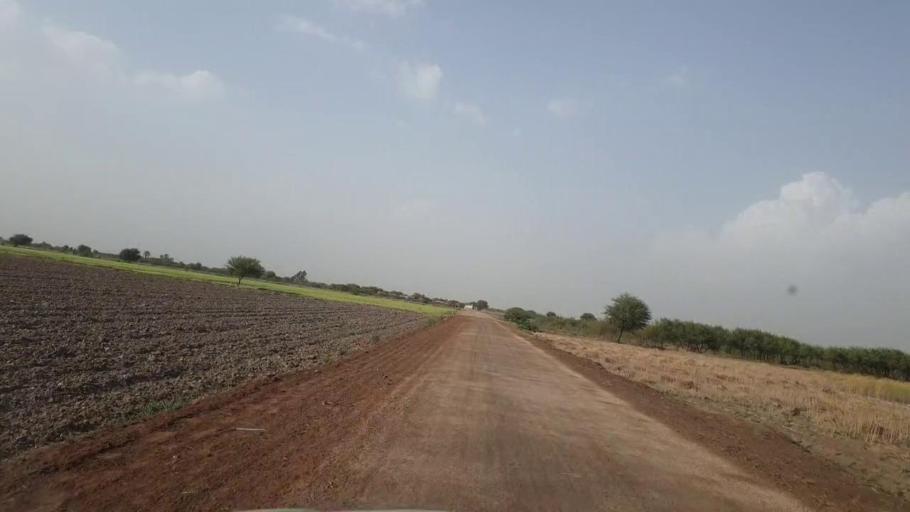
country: PK
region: Sindh
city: Tando Ghulam Ali
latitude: 25.1042
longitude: 68.8619
